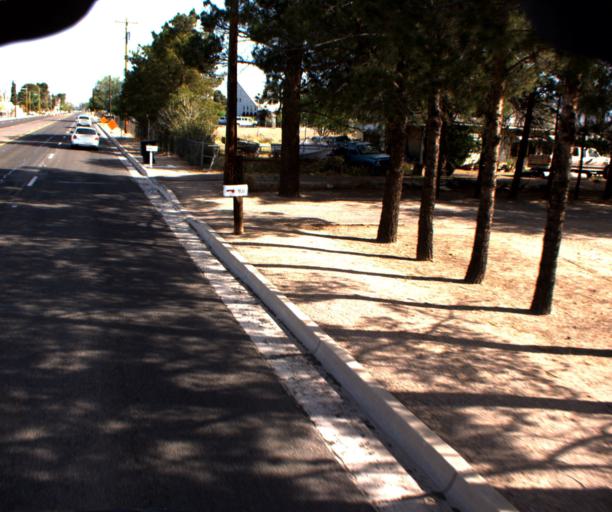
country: US
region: Arizona
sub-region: Graham County
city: Safford
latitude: 32.8189
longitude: -109.7076
